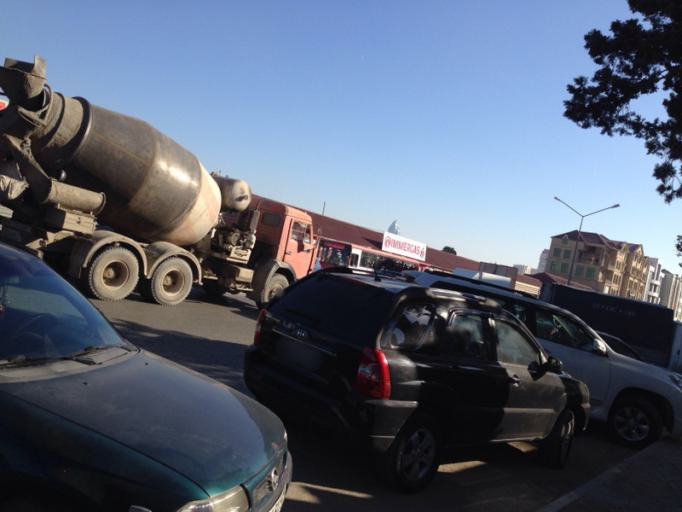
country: AZ
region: Baki
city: Baku
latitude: 40.4152
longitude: 49.8590
